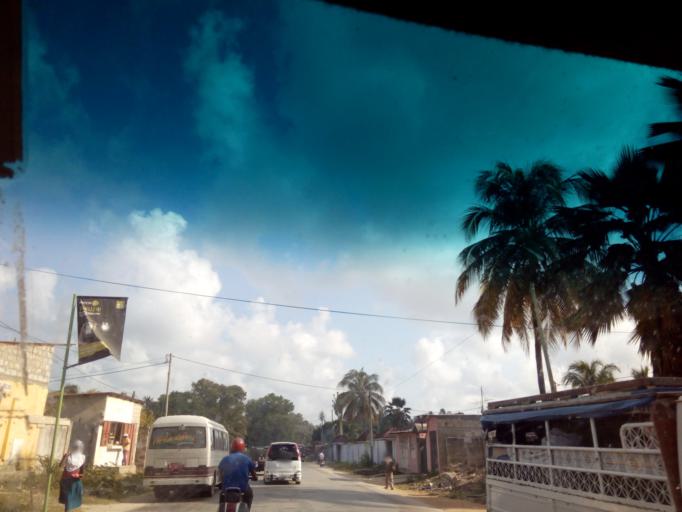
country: TZ
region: Zanzibar Urban/West
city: Zanzibar
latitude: -6.0957
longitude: 39.2191
